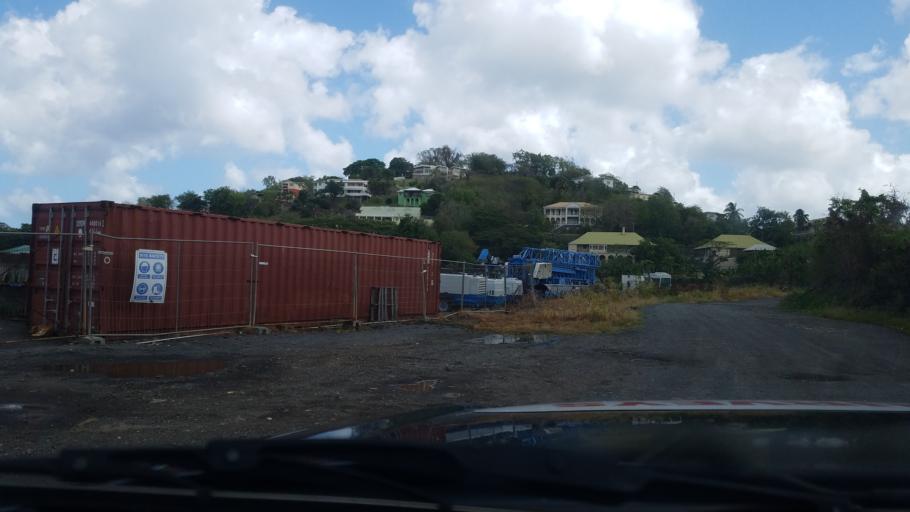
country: LC
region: Castries Quarter
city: Castries
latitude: 14.0173
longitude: -60.9980
